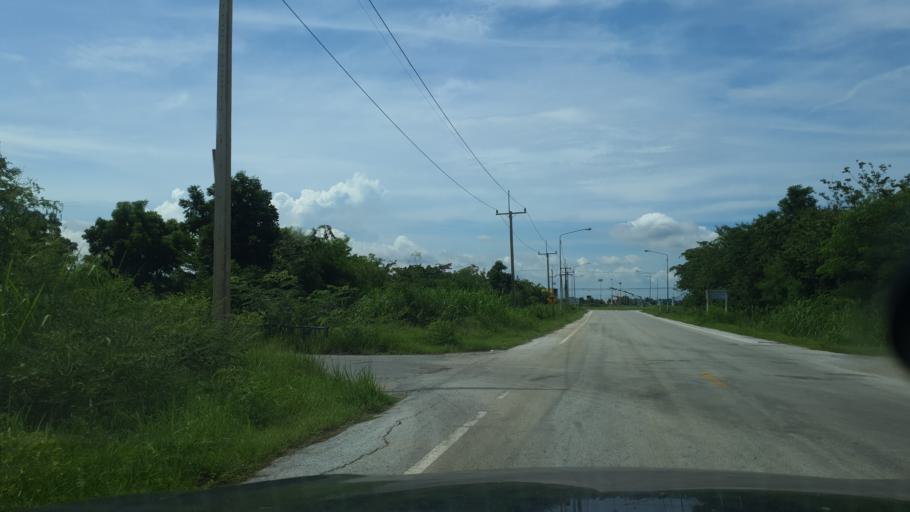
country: TH
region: Sukhothai
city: Sukhothai
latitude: 17.0703
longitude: 99.7920
